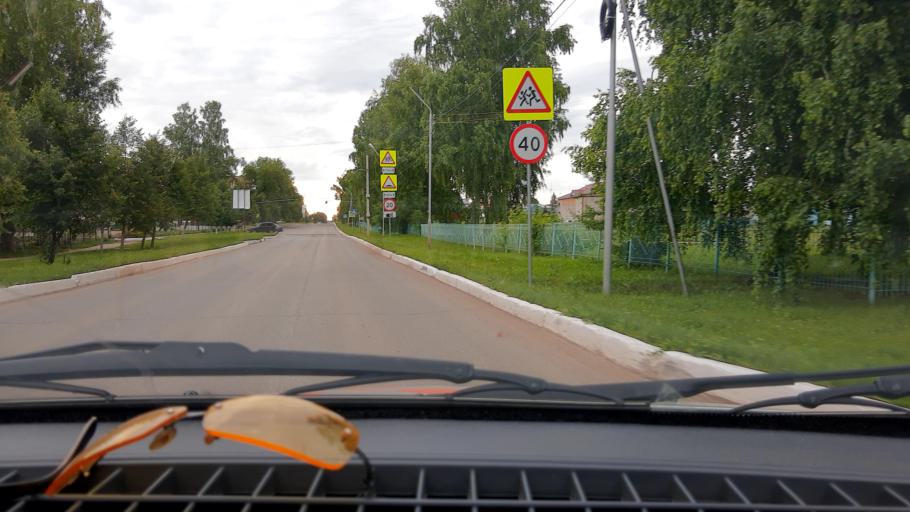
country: RU
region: Bashkortostan
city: Chishmy
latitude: 54.5864
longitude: 55.3817
